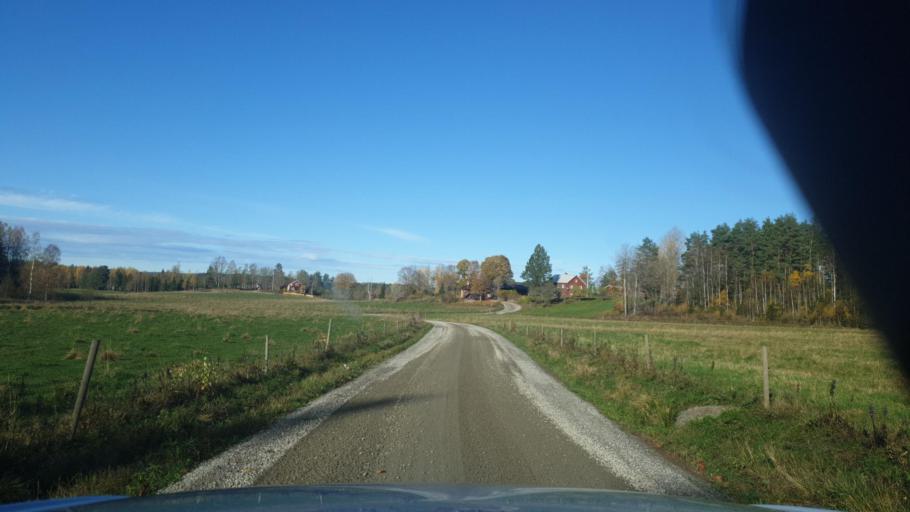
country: SE
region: Vaermland
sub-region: Arvika Kommun
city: Arvika
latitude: 59.5872
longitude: 12.8136
